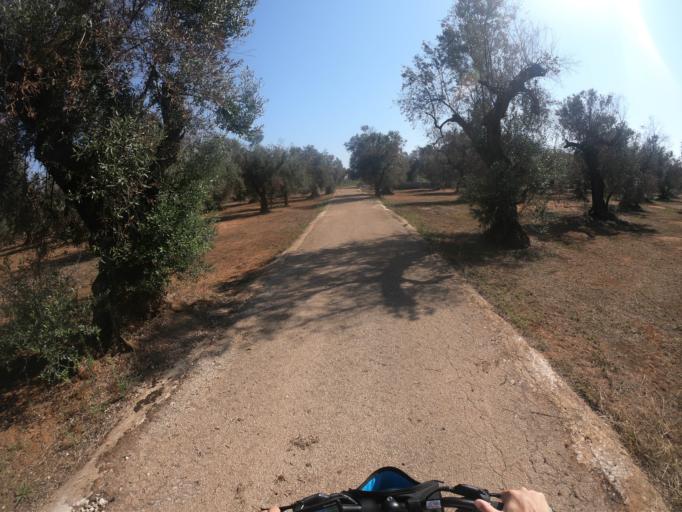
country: IT
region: Apulia
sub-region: Provincia di Lecce
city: Specchia
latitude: 39.9173
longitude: 18.2853
